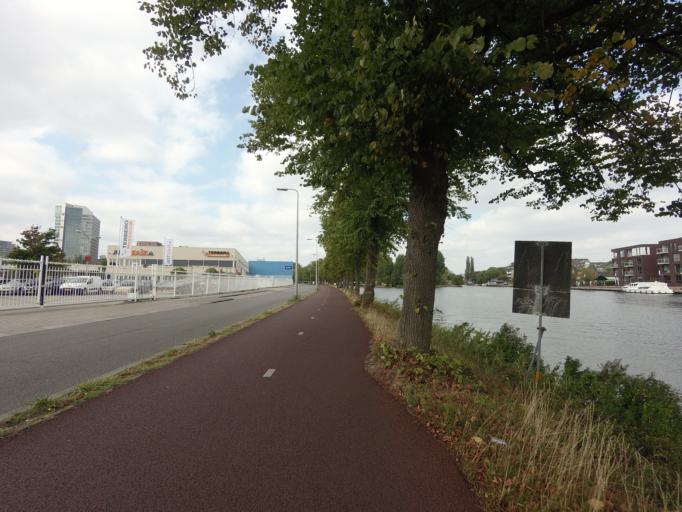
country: NL
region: Utrecht
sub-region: Gemeente Utrecht
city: Lunetten
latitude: 52.0626
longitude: 5.1124
